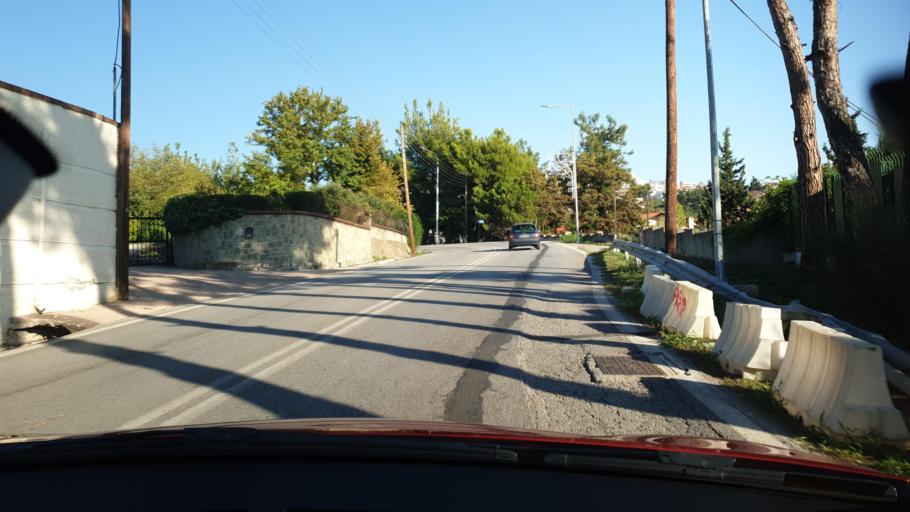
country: GR
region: Central Macedonia
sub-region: Nomos Thessalonikis
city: Panorama
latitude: 40.5920
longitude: 23.0238
